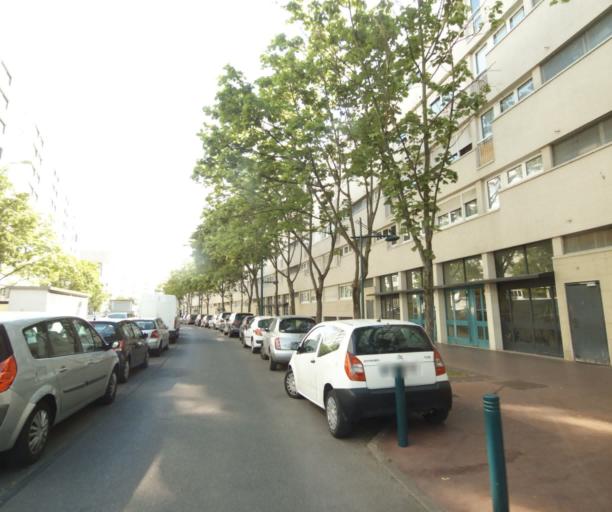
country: FR
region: Ile-de-France
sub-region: Departement des Hauts-de-Seine
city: Gennevilliers
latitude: 48.9312
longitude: 2.2858
